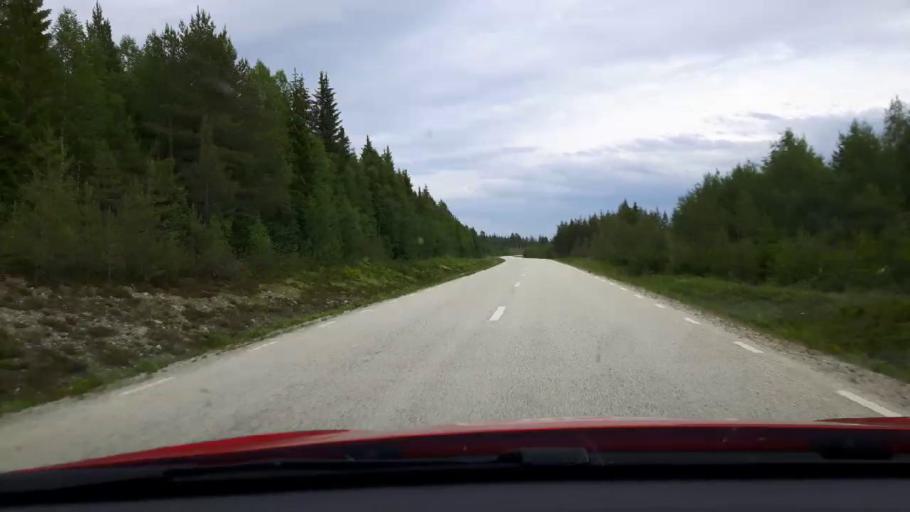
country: SE
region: Jaemtland
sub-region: Bergs Kommun
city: Hoverberg
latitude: 62.7051
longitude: 13.9439
